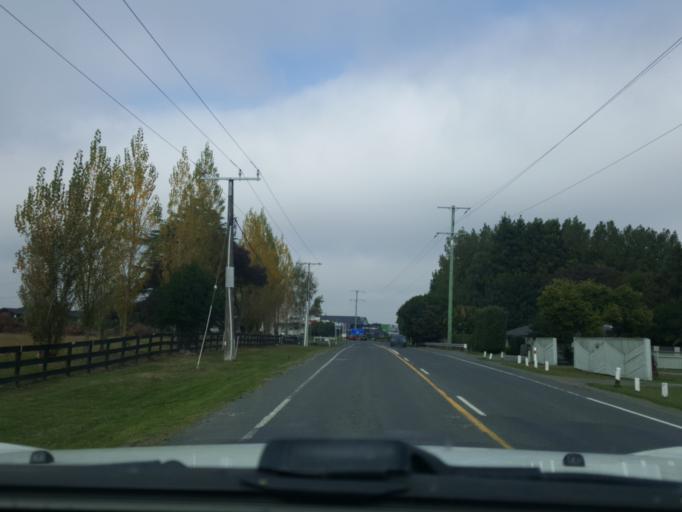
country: NZ
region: Waikato
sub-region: Hamilton City
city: Hamilton
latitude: -37.7474
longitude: 175.2929
